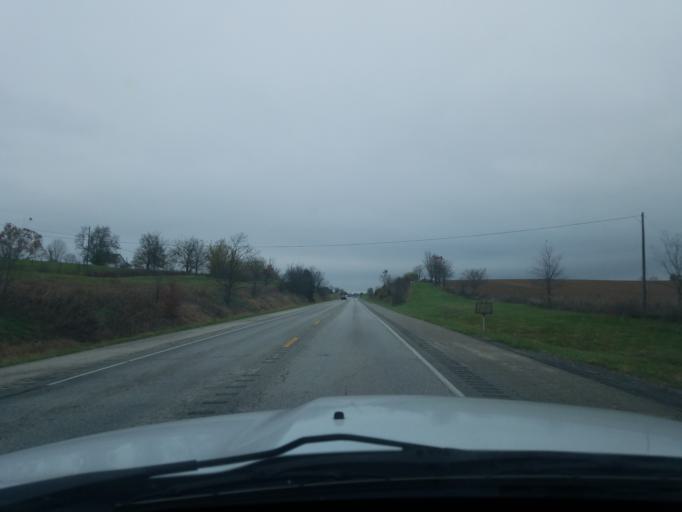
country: US
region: Kentucky
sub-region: Washington County
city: Springfield
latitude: 37.6523
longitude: -85.2407
